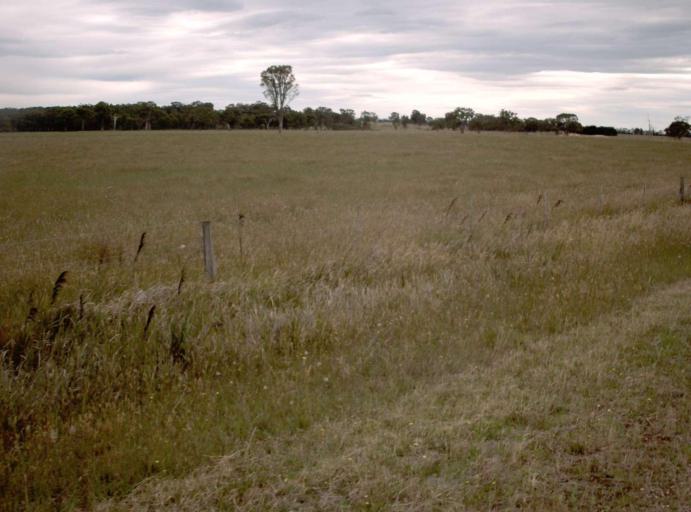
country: AU
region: Victoria
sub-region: East Gippsland
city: Bairnsdale
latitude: -37.9461
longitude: 147.5255
